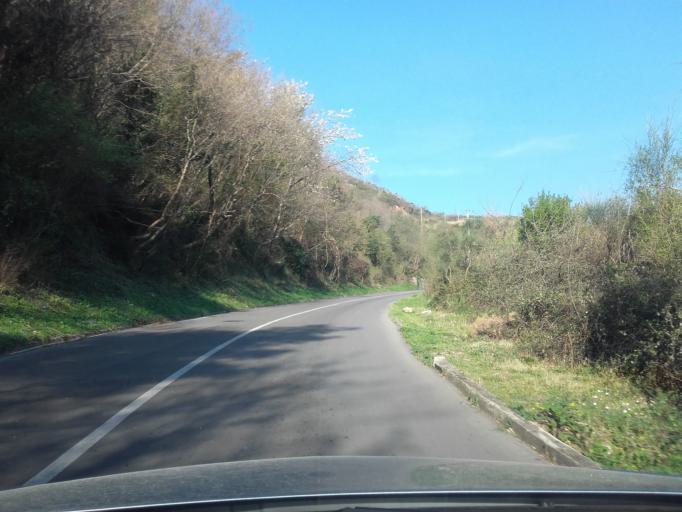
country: ME
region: Budva
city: Budva
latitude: 42.2902
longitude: 18.8271
